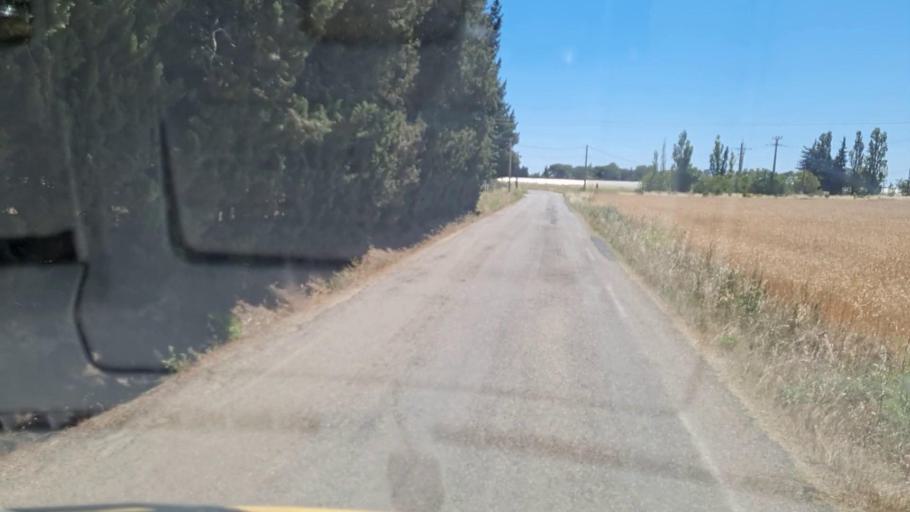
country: FR
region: Languedoc-Roussillon
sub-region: Departement du Gard
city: Le Cailar
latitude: 43.7029
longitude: 4.2321
